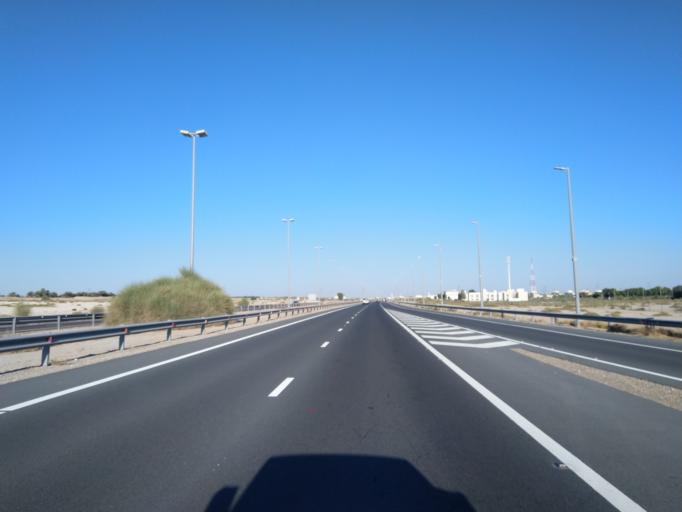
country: OM
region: Al Buraimi
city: Al Buraymi
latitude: 24.5164
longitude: 55.5010
